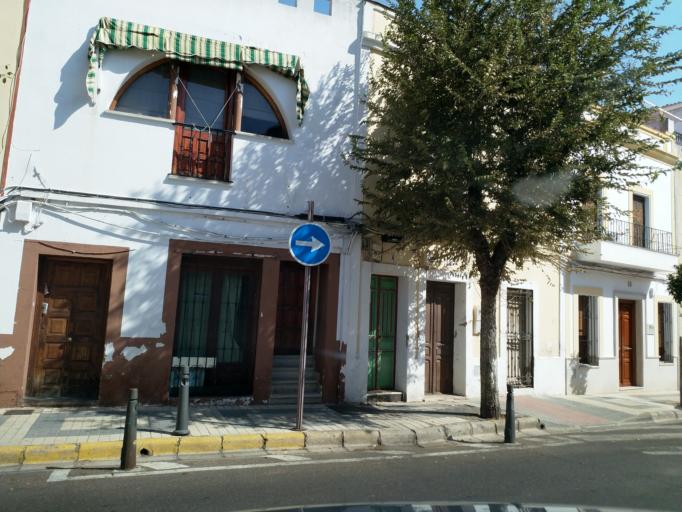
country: ES
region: Extremadura
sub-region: Provincia de Badajoz
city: Merida
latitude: 38.9176
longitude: -6.3387
